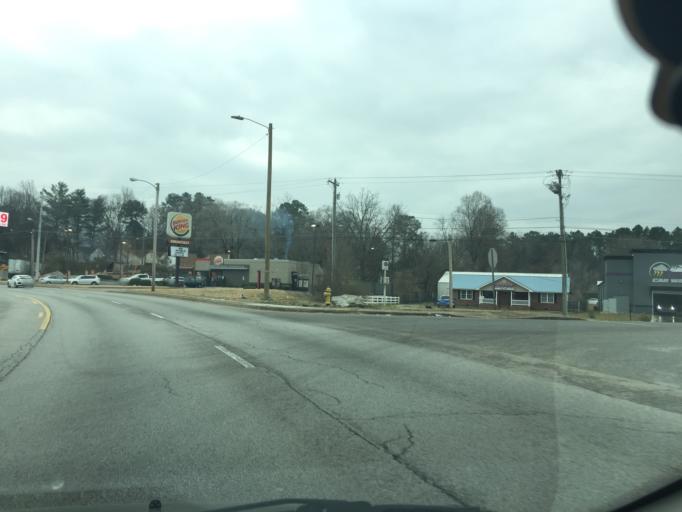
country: US
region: Tennessee
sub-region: Hamilton County
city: East Brainerd
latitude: 35.0061
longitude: -85.1536
